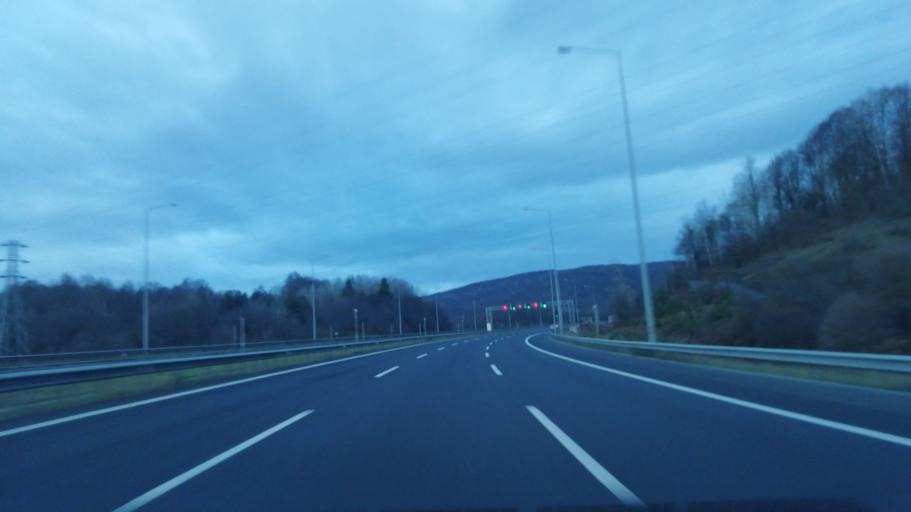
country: TR
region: Duzce
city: Kaynasli
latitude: 40.7270
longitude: 31.4454
